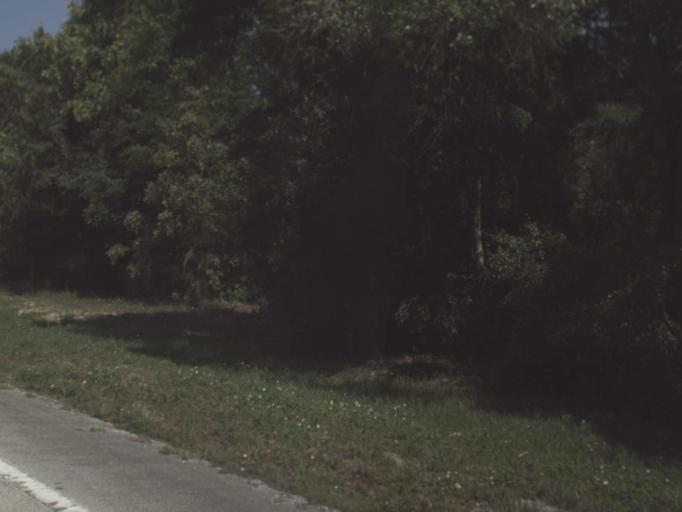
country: US
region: Florida
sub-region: Bradford County
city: Starke
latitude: 29.9821
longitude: -82.0051
